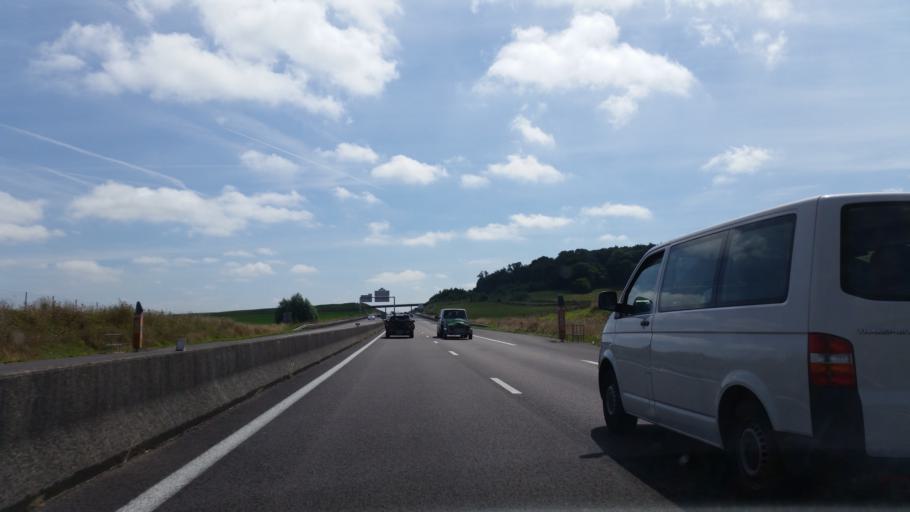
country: FR
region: Haute-Normandie
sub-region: Departement de la Seine-Maritime
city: Neufchatel-en-Bray
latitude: 49.7528
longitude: 1.5035
